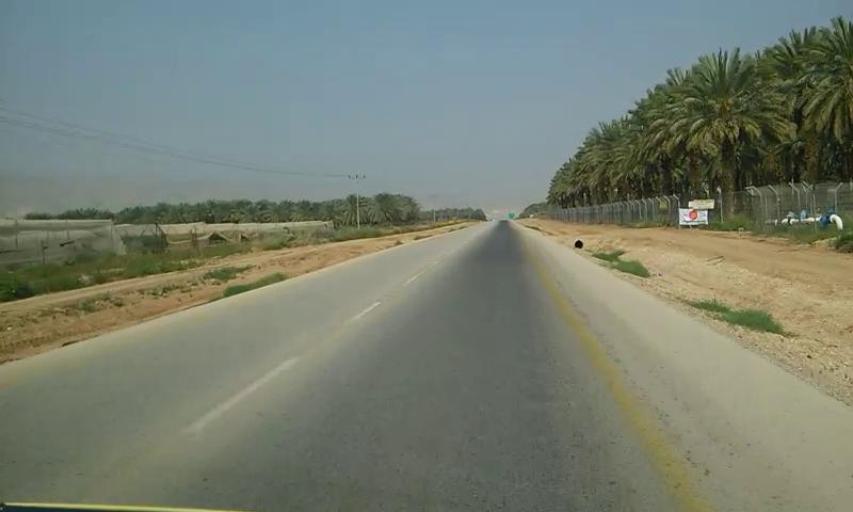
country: PS
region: West Bank
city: Al Fasayil
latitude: 31.9939
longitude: 35.4576
